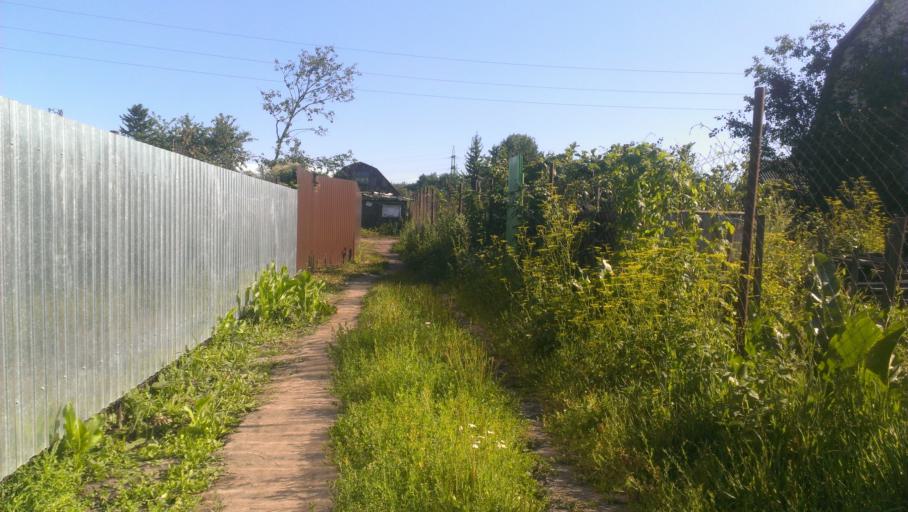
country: RU
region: Altai Krai
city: Novosilikatnyy
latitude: 53.3214
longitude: 83.6697
